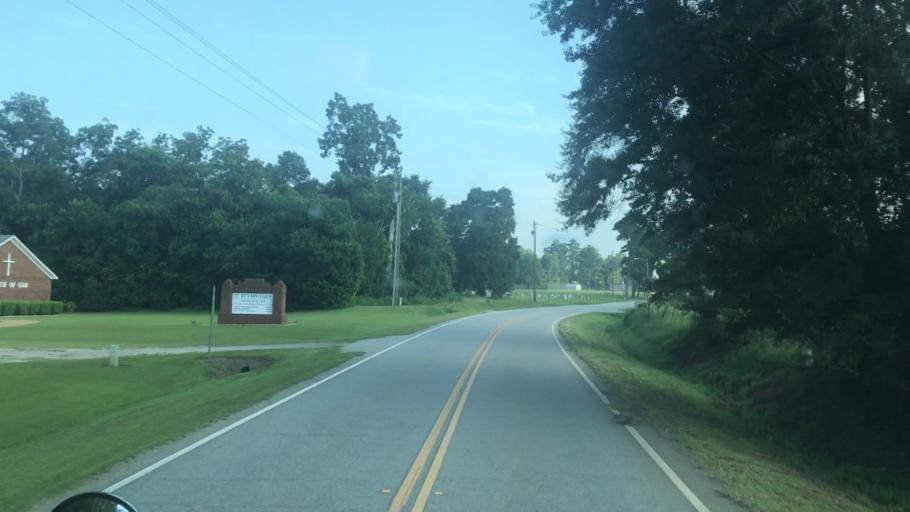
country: US
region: Florida
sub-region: Gadsden County
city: Havana
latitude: 30.7433
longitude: -84.4835
